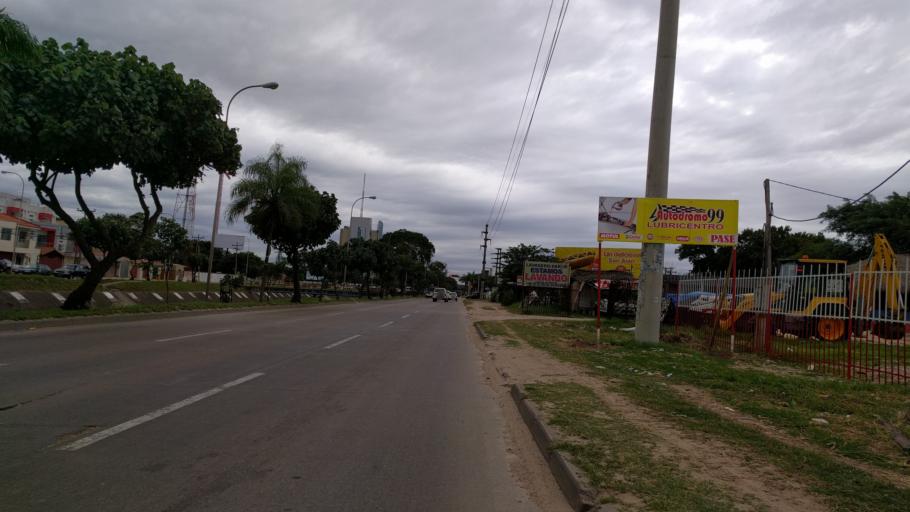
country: BO
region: Santa Cruz
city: Santa Cruz de la Sierra
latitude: -17.7884
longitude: -63.2165
